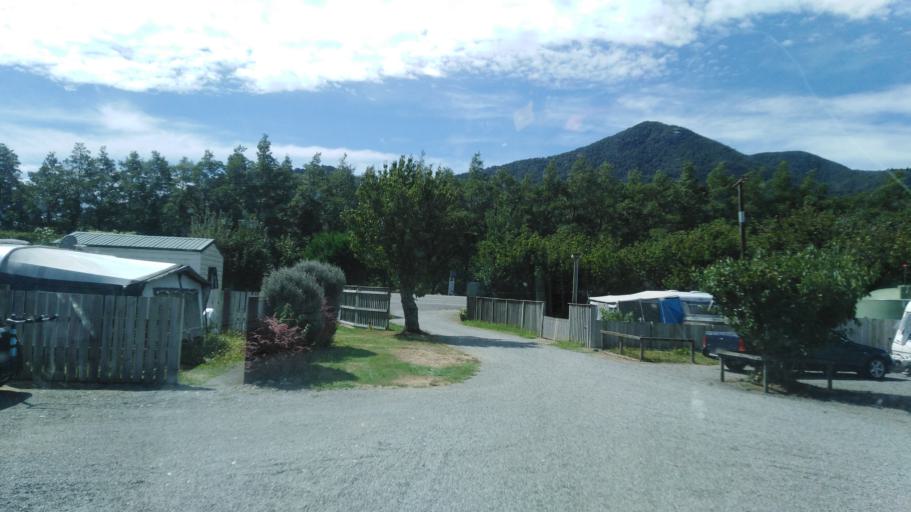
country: NZ
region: Marlborough
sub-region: Marlborough District
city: Picton
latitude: -41.3382
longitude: 173.7658
